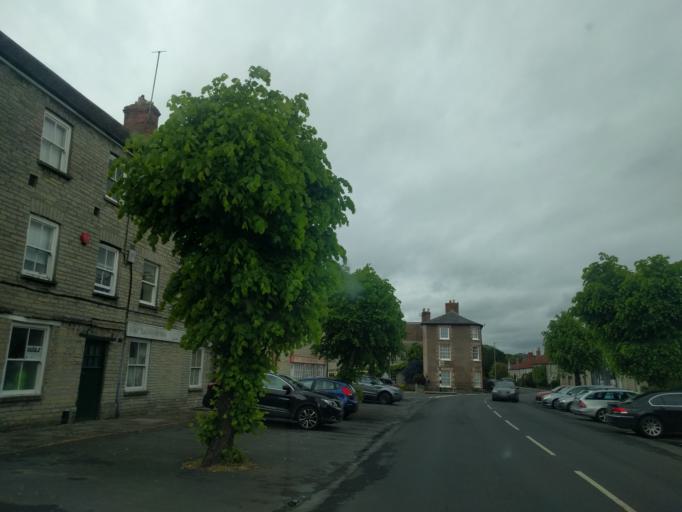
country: GB
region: England
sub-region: Somerset
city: Ilchester
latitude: 51.0545
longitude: -2.7276
